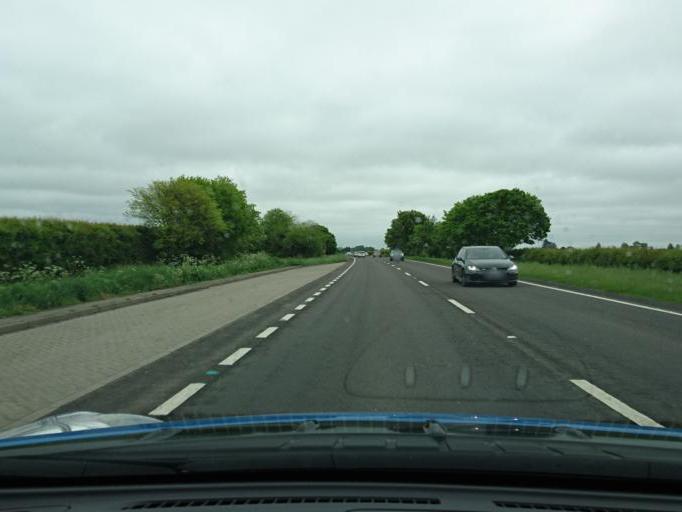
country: GB
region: England
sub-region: Oxfordshire
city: Faringdon
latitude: 51.6584
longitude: -1.5654
